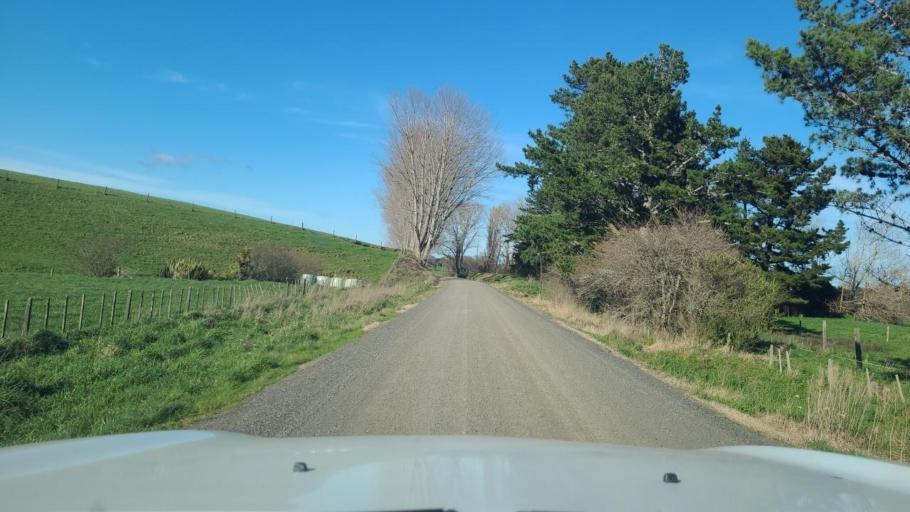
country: NZ
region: Bay of Plenty
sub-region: Western Bay of Plenty District
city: Katikati
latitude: -37.6111
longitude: 175.7962
